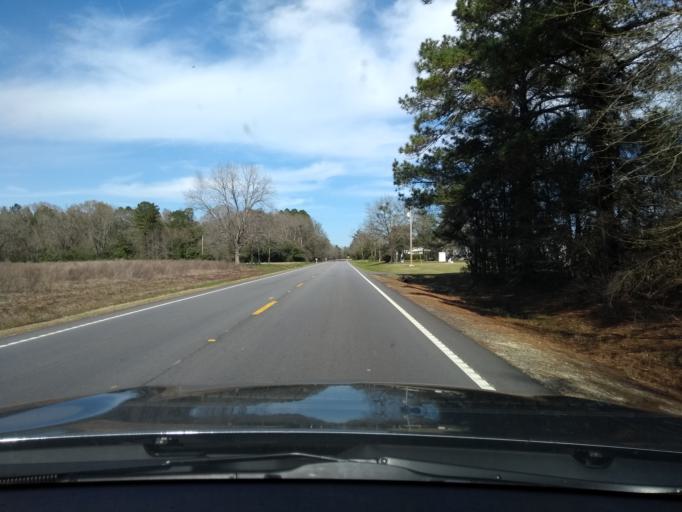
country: US
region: Georgia
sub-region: Bulloch County
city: Brooklet
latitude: 32.4744
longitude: -81.6049
